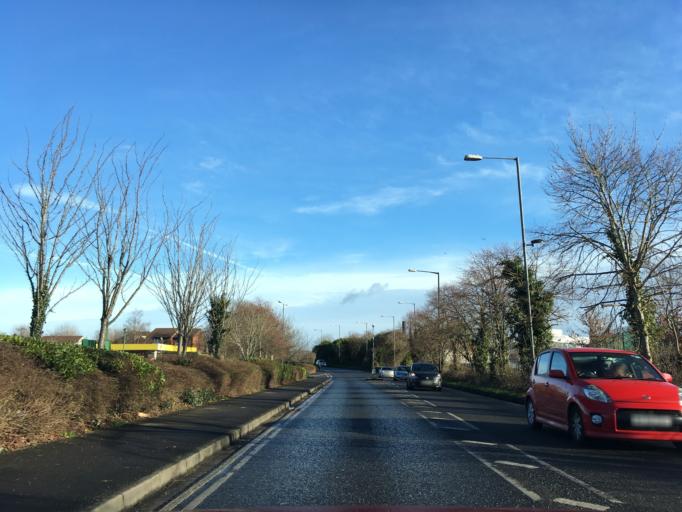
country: GB
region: England
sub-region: South Gloucestershire
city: Mangotsfield
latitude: 51.4776
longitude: -2.5318
